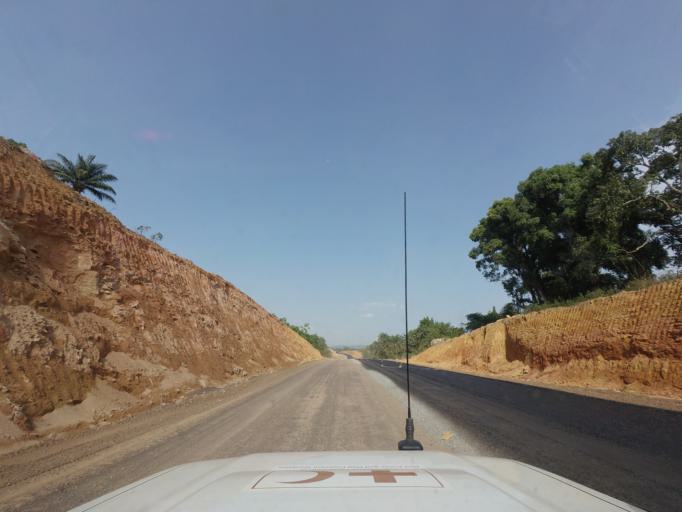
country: LR
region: Margibi
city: Kakata
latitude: 6.7506
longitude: -10.0882
